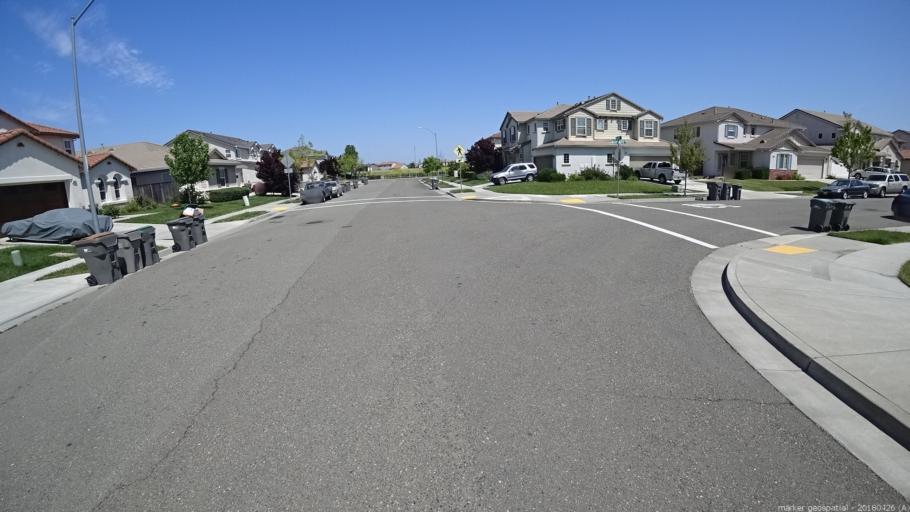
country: US
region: California
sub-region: Yolo County
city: West Sacramento
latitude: 38.5328
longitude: -121.5810
